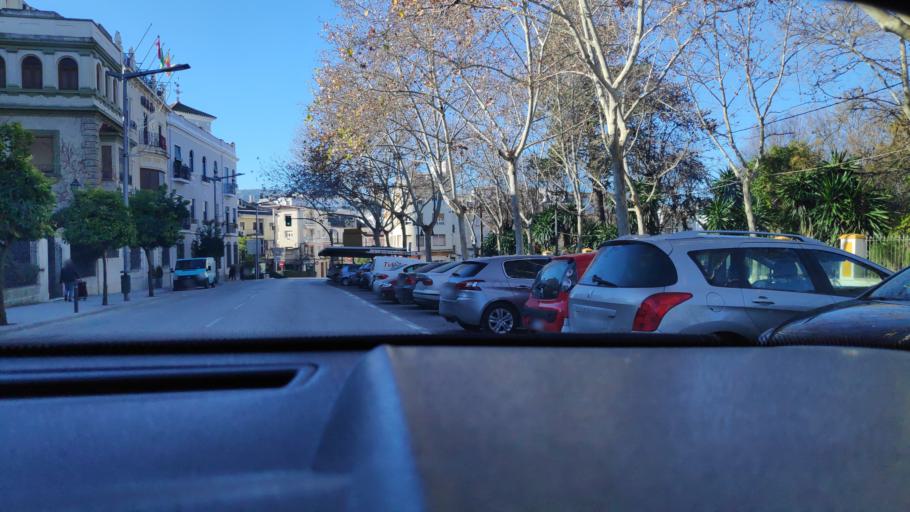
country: ES
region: Andalusia
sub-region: Province of Cordoba
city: Baena
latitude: 37.6166
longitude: -4.3203
